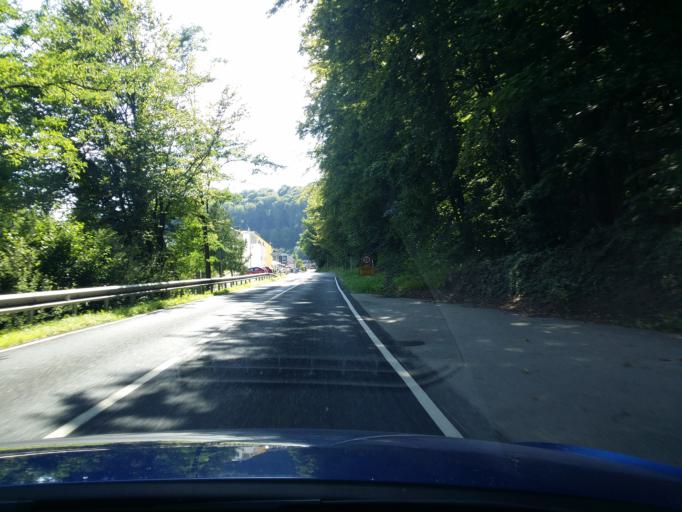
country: LU
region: Luxembourg
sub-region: Canton de Capellen
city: Kopstal
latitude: 49.6722
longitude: 6.0781
